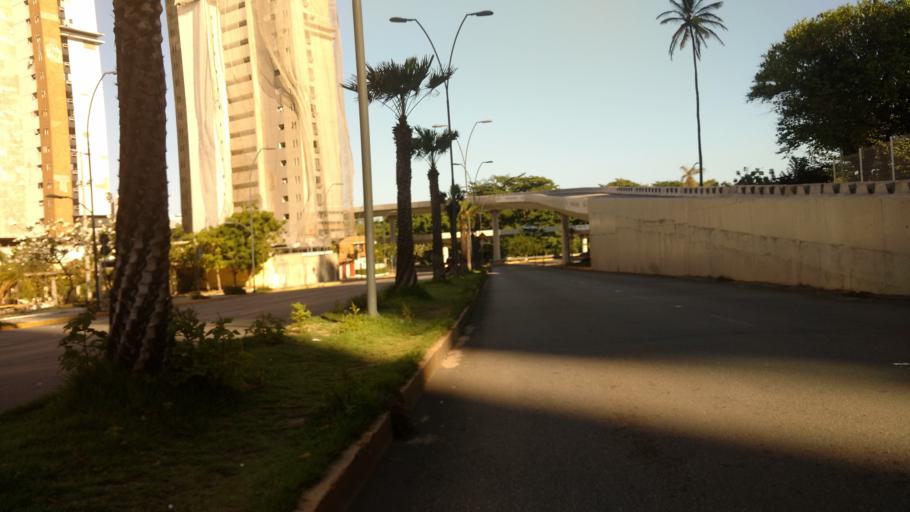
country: BR
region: Ceara
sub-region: Fortaleza
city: Fortaleza
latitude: -3.7488
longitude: -38.4915
